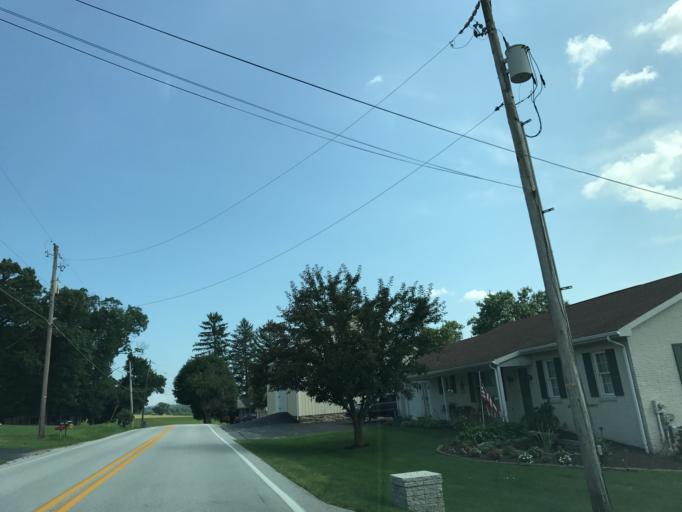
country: US
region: Pennsylvania
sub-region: York County
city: Pennville
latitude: 39.7485
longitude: -77.0241
